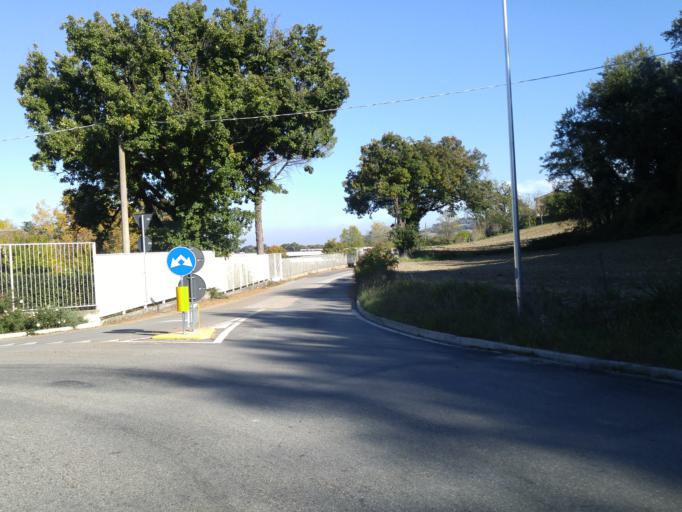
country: IT
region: The Marches
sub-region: Provincia di Pesaro e Urbino
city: Sant'Ippolito
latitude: 43.7013
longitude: 12.8728
